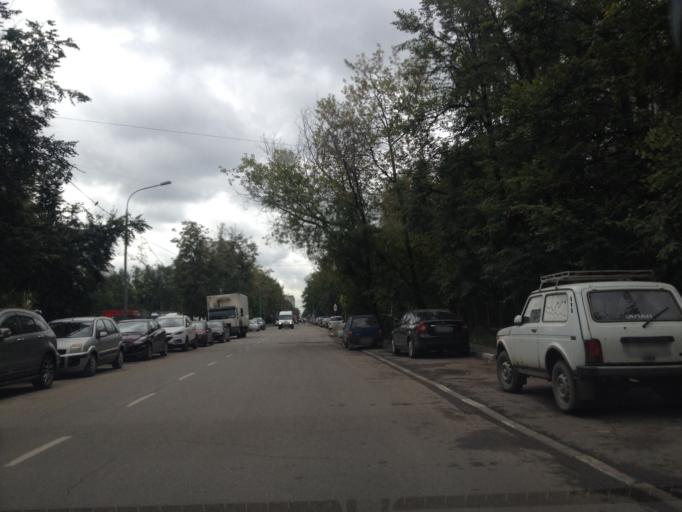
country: RU
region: Moscow
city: Gol'yanovo
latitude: 55.8096
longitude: 37.8048
